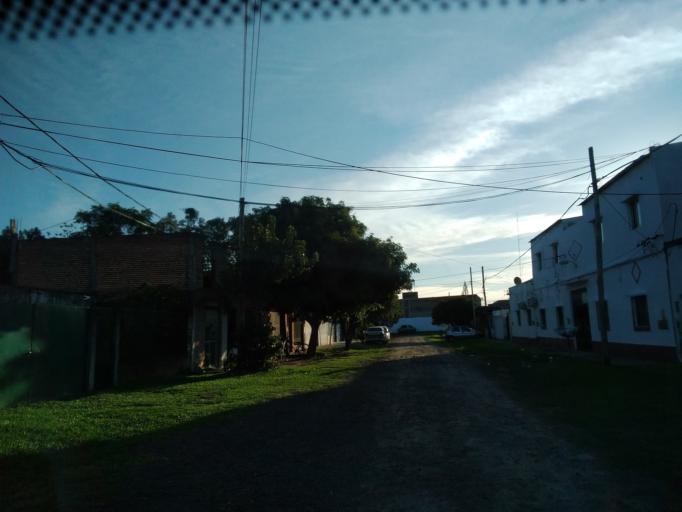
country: AR
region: Corrientes
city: Corrientes
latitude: -27.4621
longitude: -58.7851
